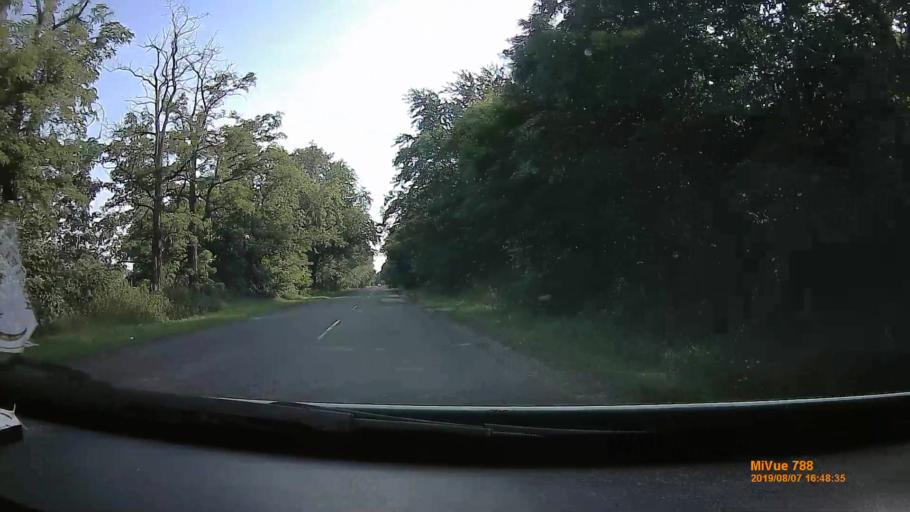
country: HU
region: Borsod-Abauj-Zemplen
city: Abaujszanto
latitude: 48.3299
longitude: 21.2033
